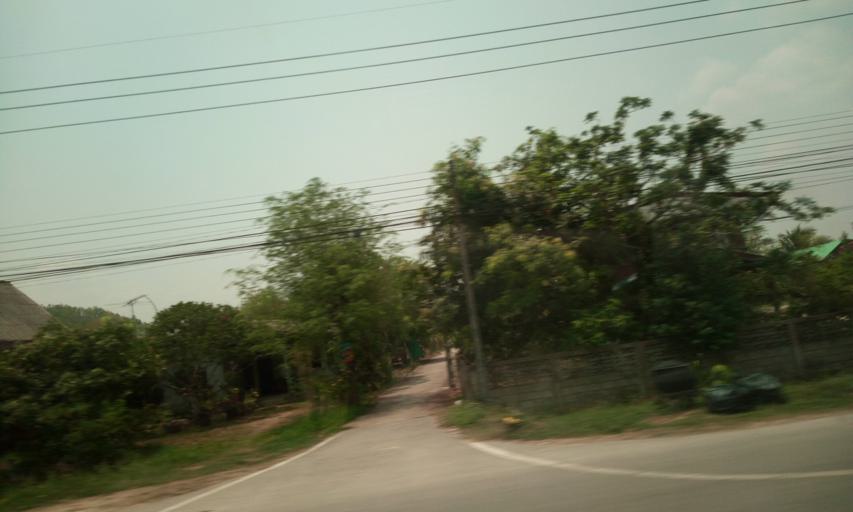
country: TH
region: Chiang Rai
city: Thoeng
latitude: 19.6881
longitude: 100.1388
